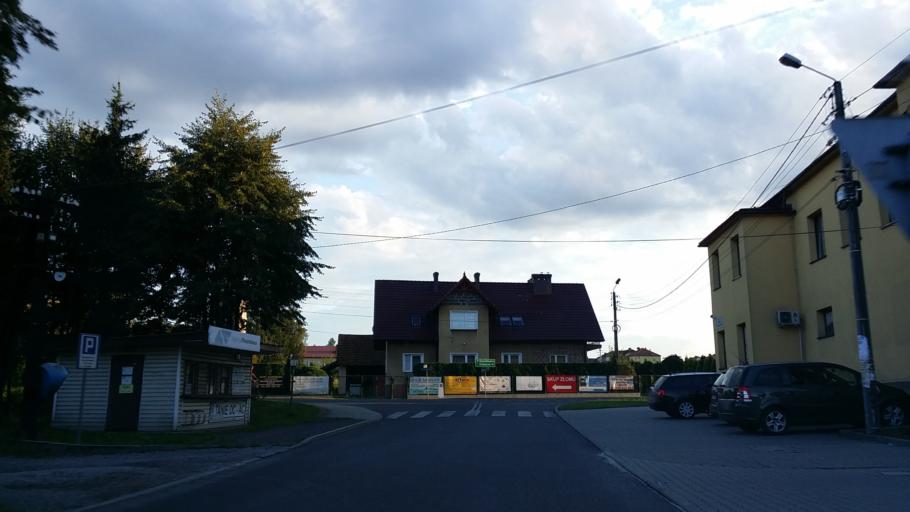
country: PL
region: Lesser Poland Voivodeship
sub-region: Powiat oswiecimski
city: Osiek
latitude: 49.9510
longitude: 19.2648
